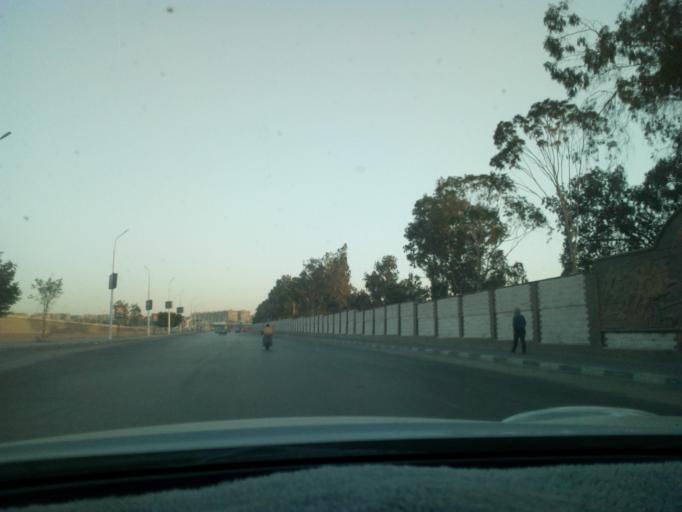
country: EG
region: Muhafazat al Qalyubiyah
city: Al Khankah
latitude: 30.1156
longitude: 31.3652
